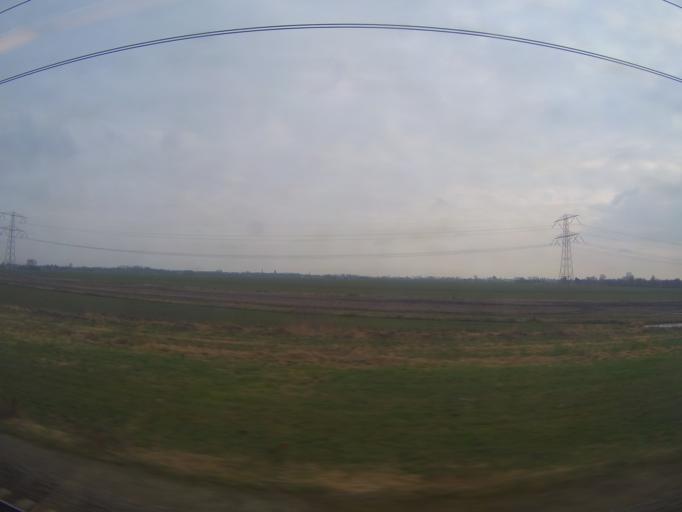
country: NL
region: Utrecht
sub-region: Gemeente Oudewater
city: Oudewater
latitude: 52.0400
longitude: 4.8409
